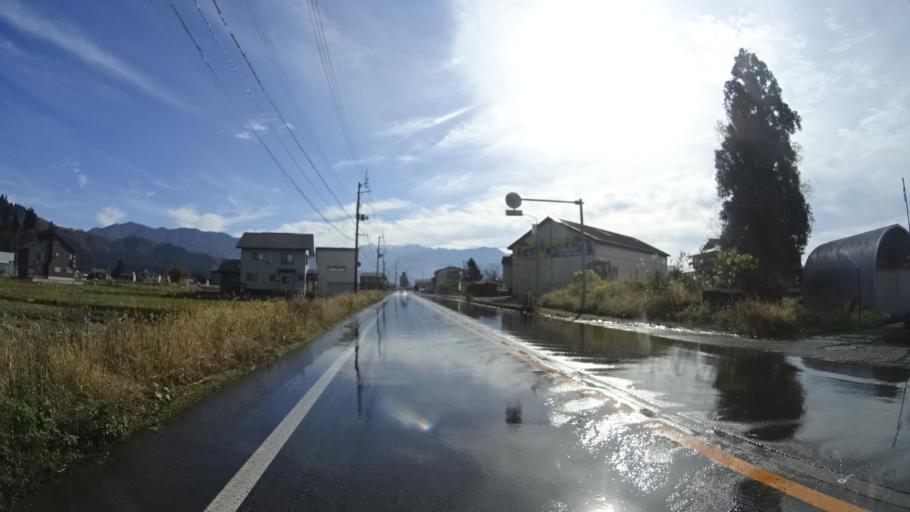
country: JP
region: Niigata
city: Muikamachi
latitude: 37.1140
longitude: 138.9208
